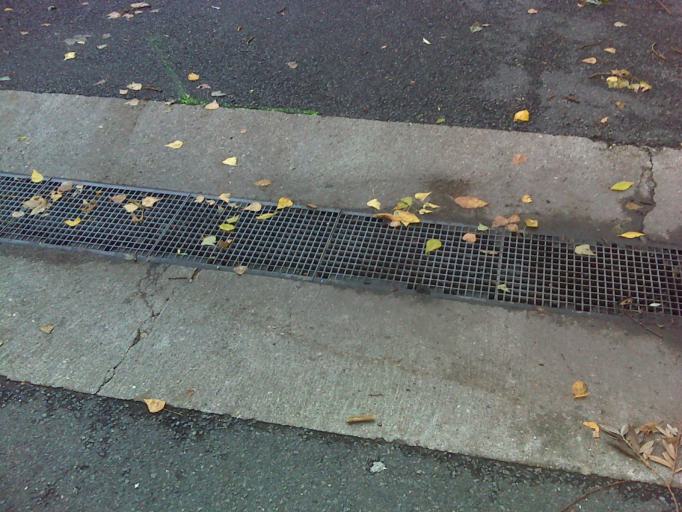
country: FR
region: Bourgogne
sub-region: Departement de la Nievre
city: La Charite-sur-Loire
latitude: 47.1744
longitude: 3.0114
